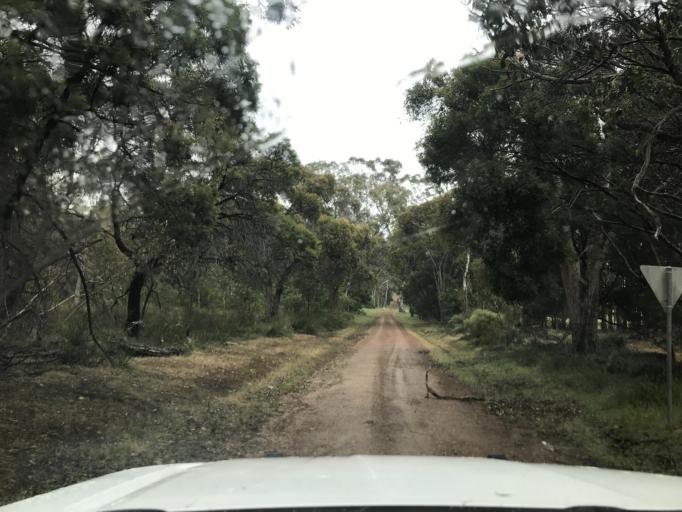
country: AU
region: South Australia
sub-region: Wattle Range
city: Penola
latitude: -37.2539
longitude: 141.3402
